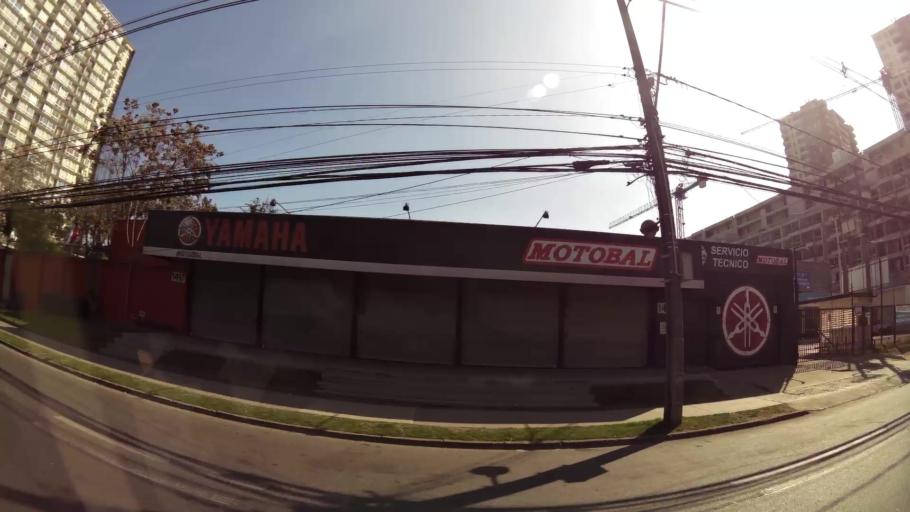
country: CL
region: Santiago Metropolitan
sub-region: Provincia de Santiago
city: Santiago
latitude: -33.4657
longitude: -70.6240
